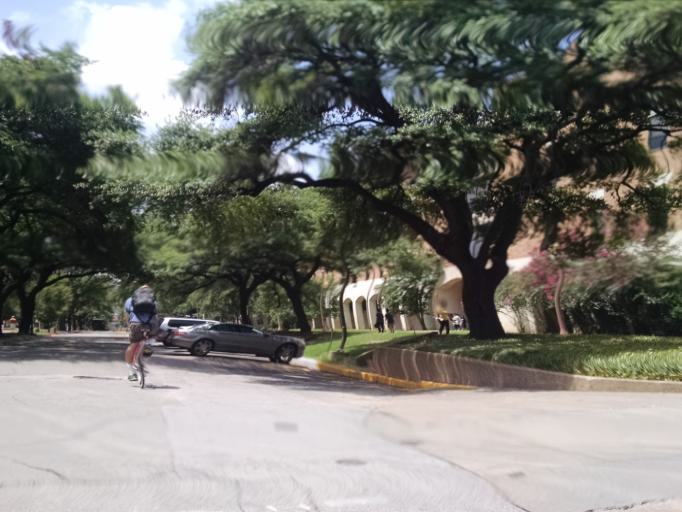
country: US
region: Texas
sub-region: Travis County
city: Austin
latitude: 30.2867
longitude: -97.7372
